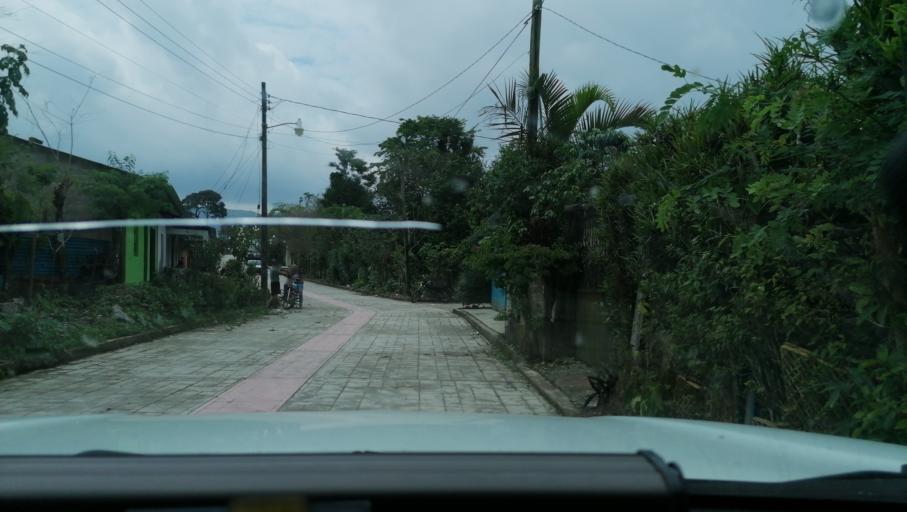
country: MX
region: Chiapas
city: Ixtacomitan
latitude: 17.3371
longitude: -93.1292
